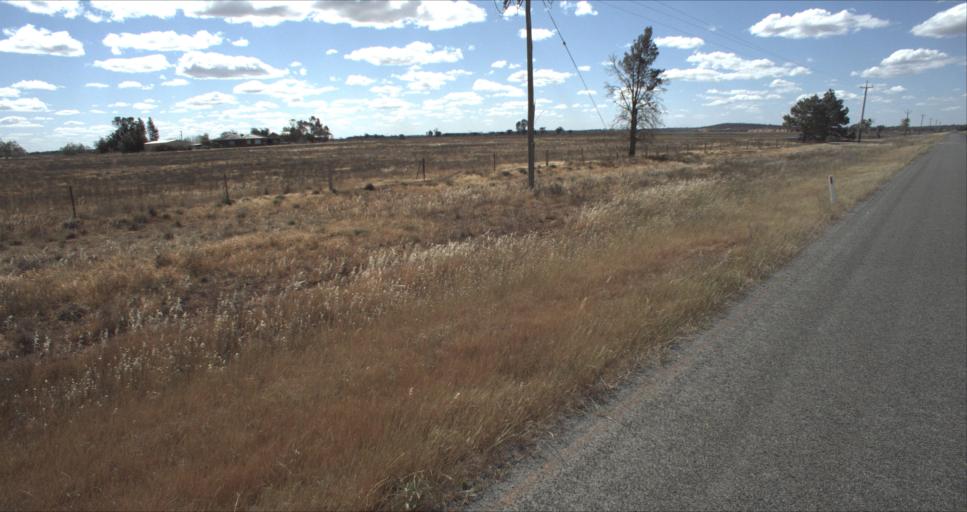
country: AU
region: New South Wales
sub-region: Leeton
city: Leeton
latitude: -34.4582
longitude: 146.2532
